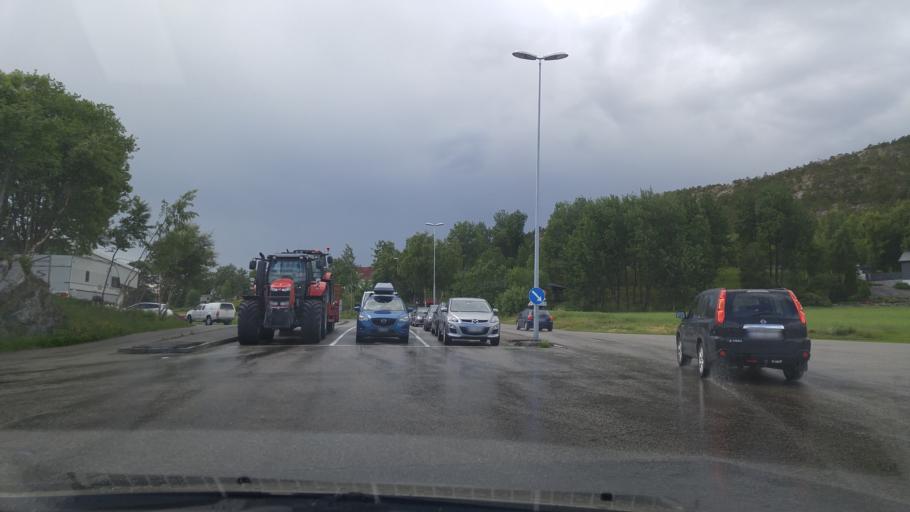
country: NO
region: Nord-Trondelag
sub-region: Naeroy
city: Kolvereid
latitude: 64.8275
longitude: 11.6121
